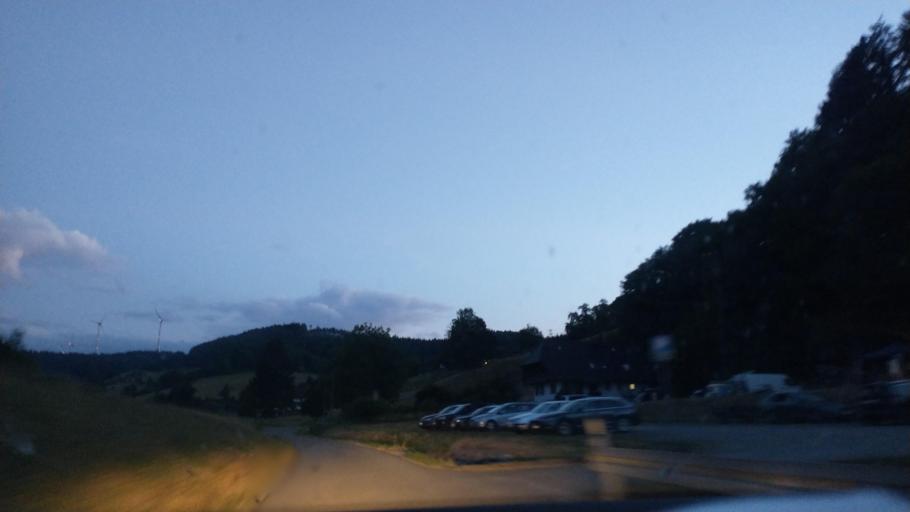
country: DE
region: Baden-Wuerttemberg
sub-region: Freiburg Region
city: Biberach
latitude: 48.3175
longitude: 7.9994
